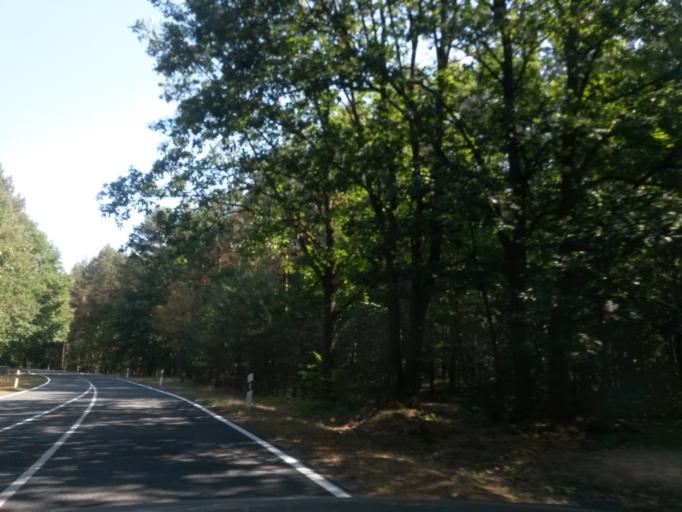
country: DE
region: Brandenburg
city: Wiesenburg
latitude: 52.0764
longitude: 12.4057
